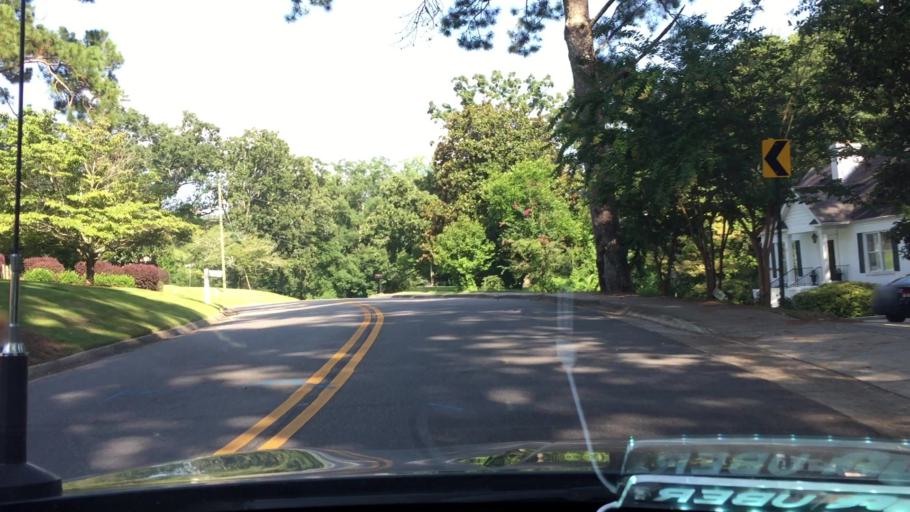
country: US
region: Alabama
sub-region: Lee County
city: Auburn
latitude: 32.6015
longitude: -85.4733
